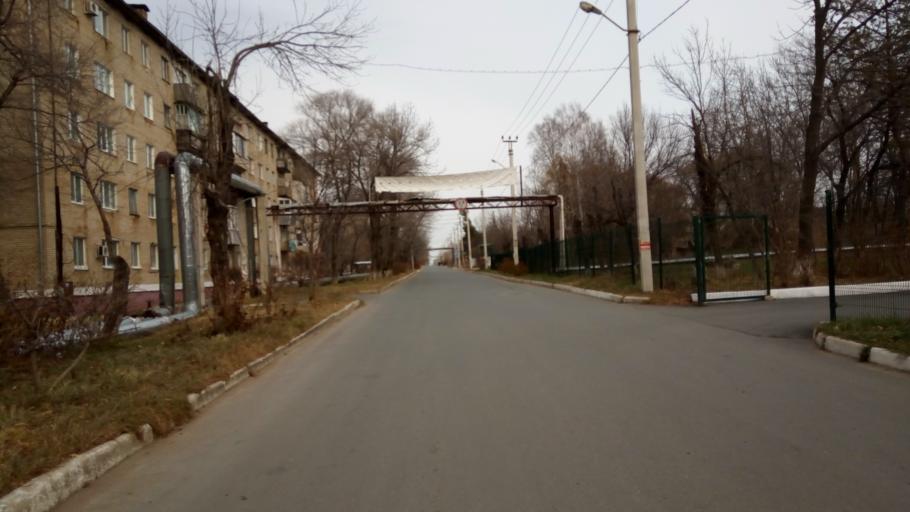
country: RU
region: Primorskiy
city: Novoshakhtinskiy
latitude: 44.0253
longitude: 132.1619
